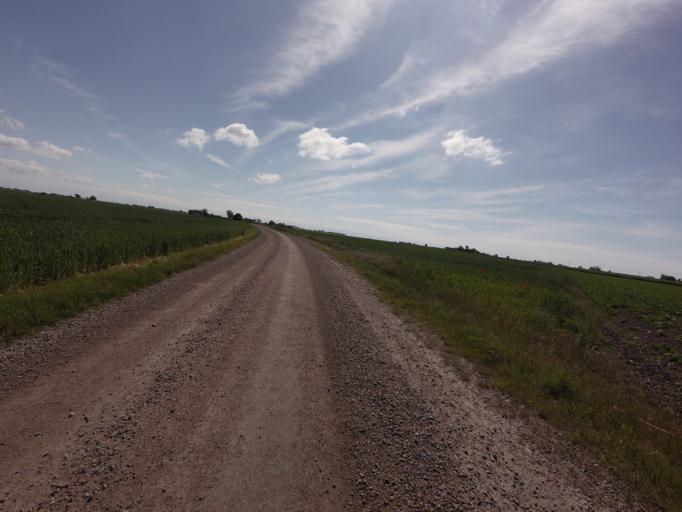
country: SE
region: Skane
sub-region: Trelleborgs Kommun
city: Skare
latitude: 55.4145
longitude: 13.0371
